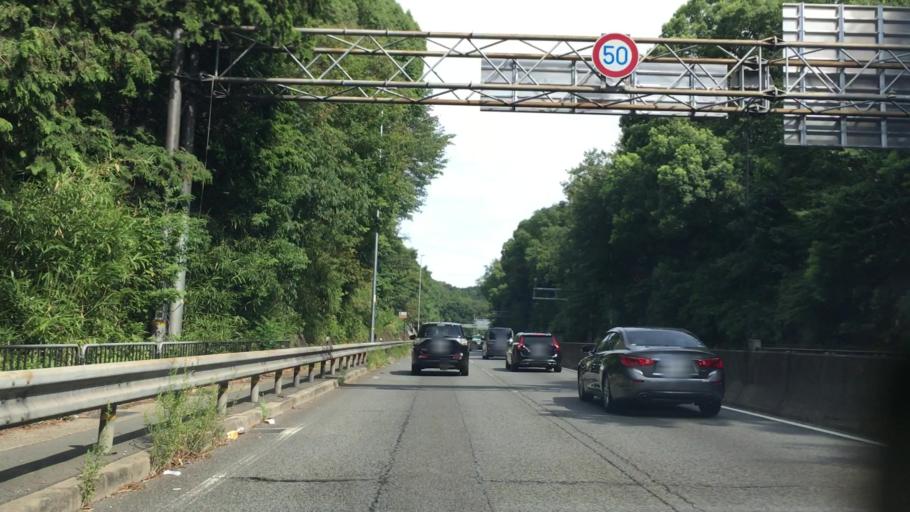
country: JP
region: Kyoto
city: Kyoto
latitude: 34.9922
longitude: 135.7808
